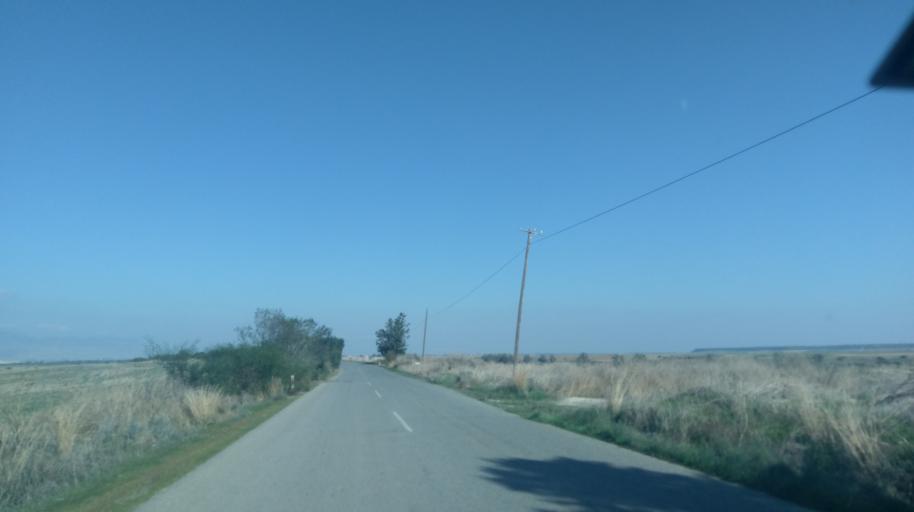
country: CY
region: Larnaka
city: Athienou
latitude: 35.1023
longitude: 33.4945
